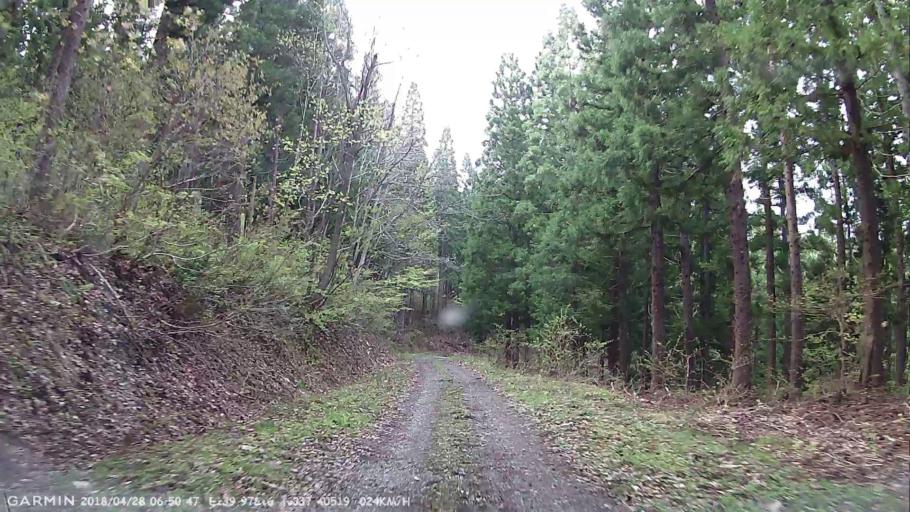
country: JP
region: Fukushima
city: Inawashiro
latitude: 37.4051
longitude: 139.9782
